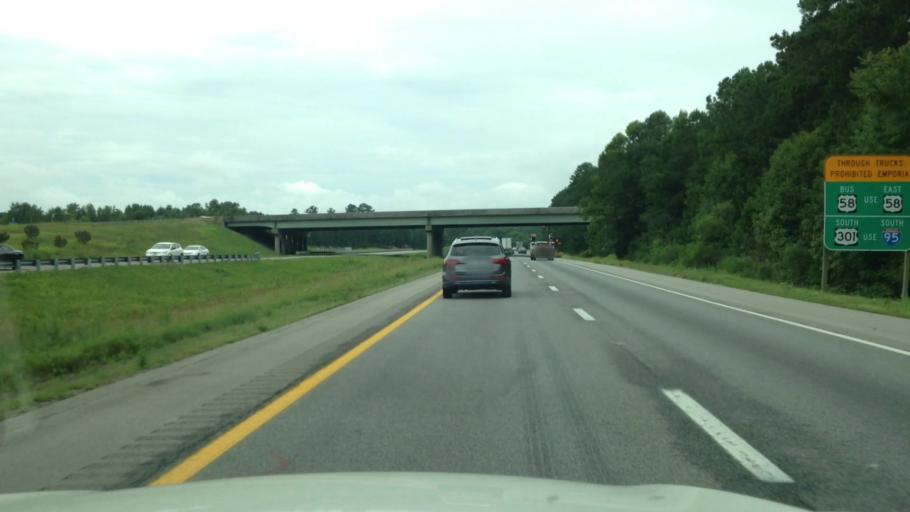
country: US
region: Virginia
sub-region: City of Emporia
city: Emporia
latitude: 36.7350
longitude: -77.5211
